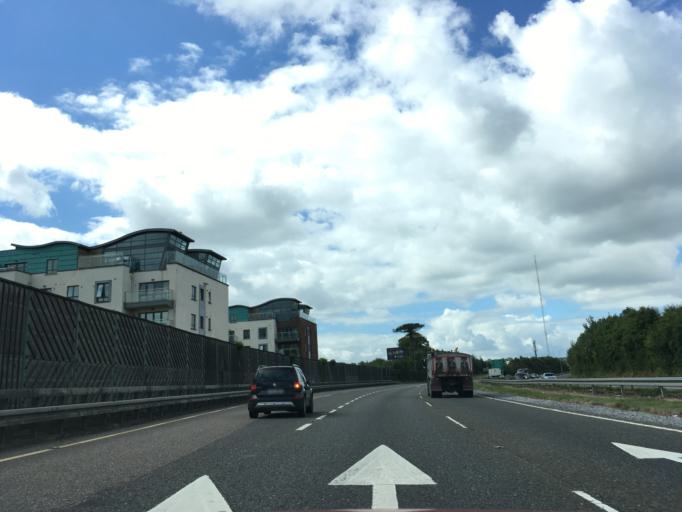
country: IE
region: Munster
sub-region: County Cork
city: Passage West
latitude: 51.8860
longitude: -8.3924
